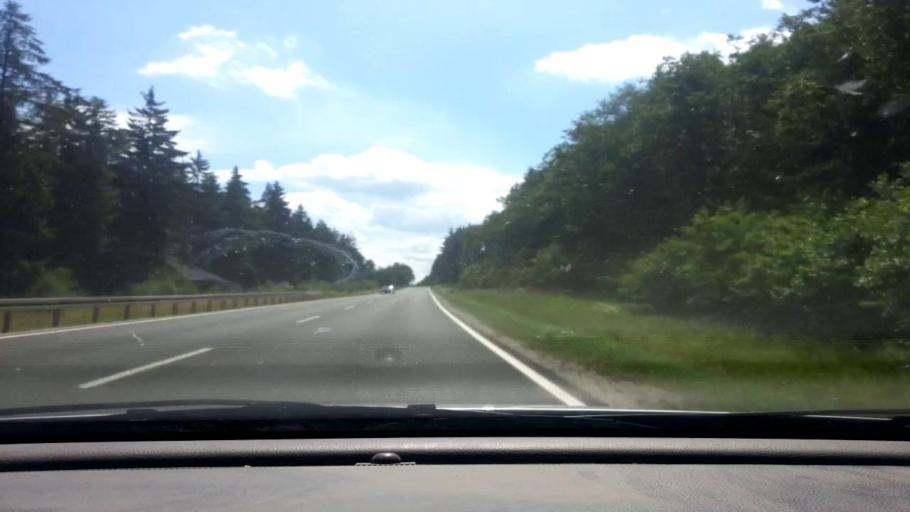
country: DE
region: Bavaria
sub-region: Upper Palatinate
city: Erbendorf
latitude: 49.8436
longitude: 12.0023
